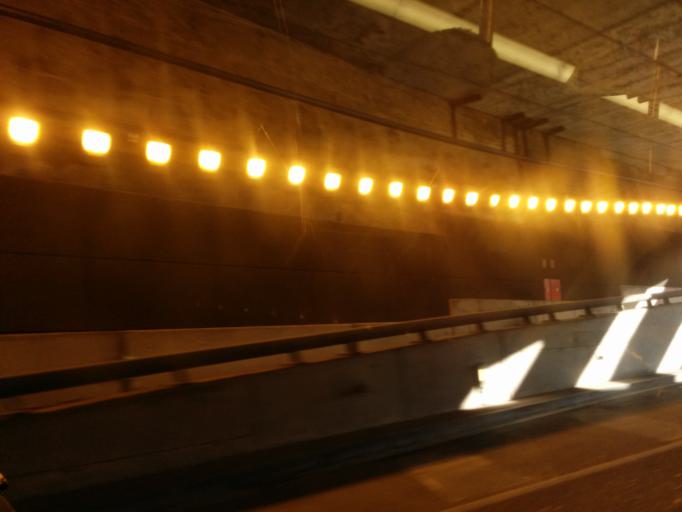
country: ES
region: Catalonia
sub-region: Provincia de Barcelona
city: L'Hospitalet de Llobregat
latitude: 41.3576
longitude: 2.1259
